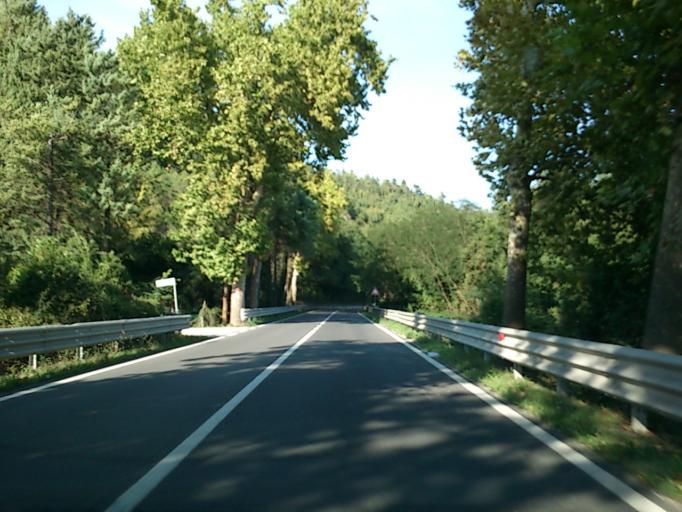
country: IT
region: The Marches
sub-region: Provincia di Pesaro e Urbino
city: Fermignano
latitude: 43.6958
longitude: 12.6711
